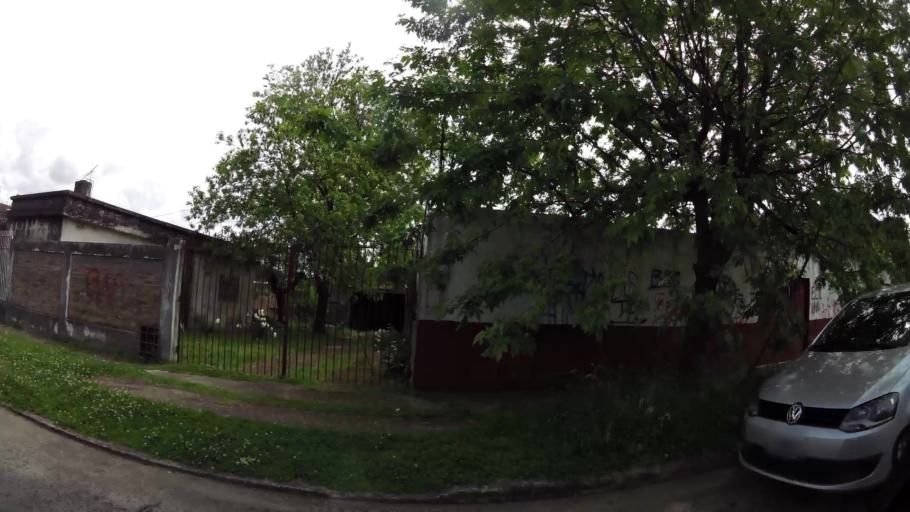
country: AR
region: Buenos Aires
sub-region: Partido de Quilmes
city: Quilmes
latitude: -34.7757
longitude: -58.2777
